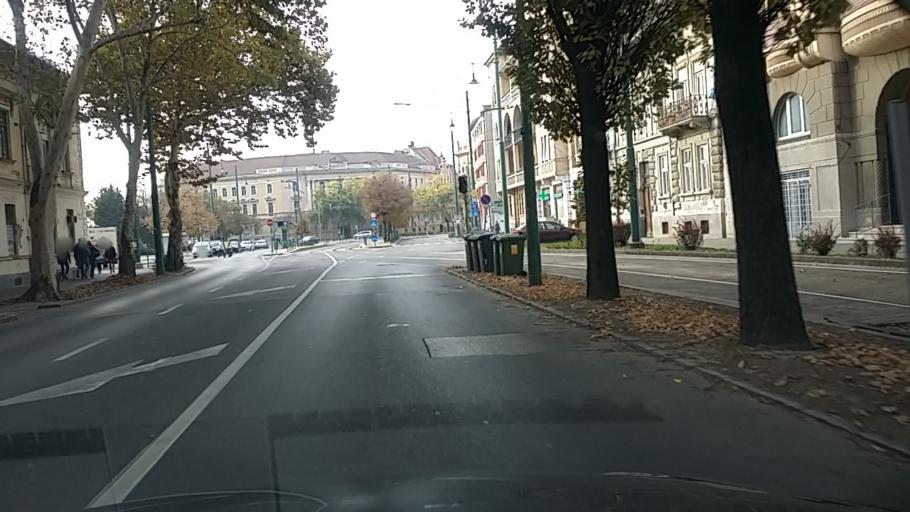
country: HU
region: Csongrad
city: Szeged
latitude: 46.2576
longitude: 20.1564
